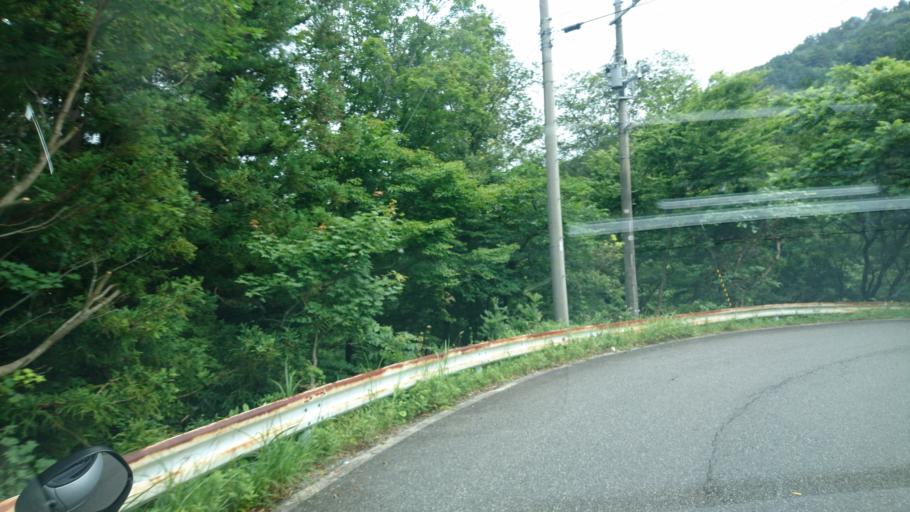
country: JP
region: Iwate
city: Ofunato
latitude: 39.1336
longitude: 141.7866
